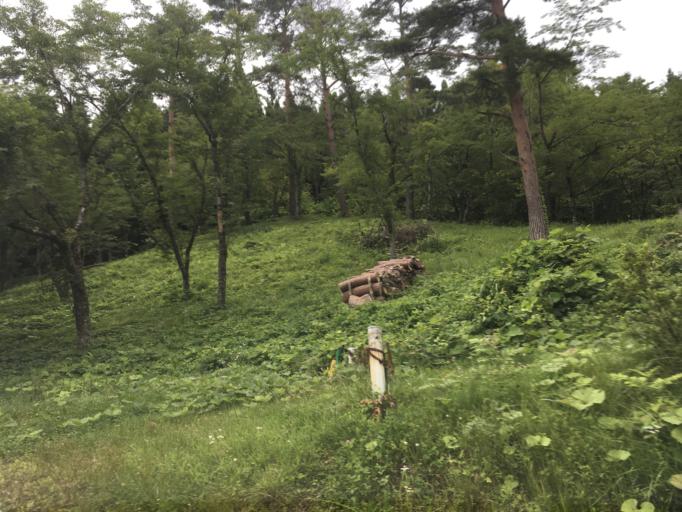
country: JP
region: Iwate
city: Ichinoseki
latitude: 38.8687
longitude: 141.3989
